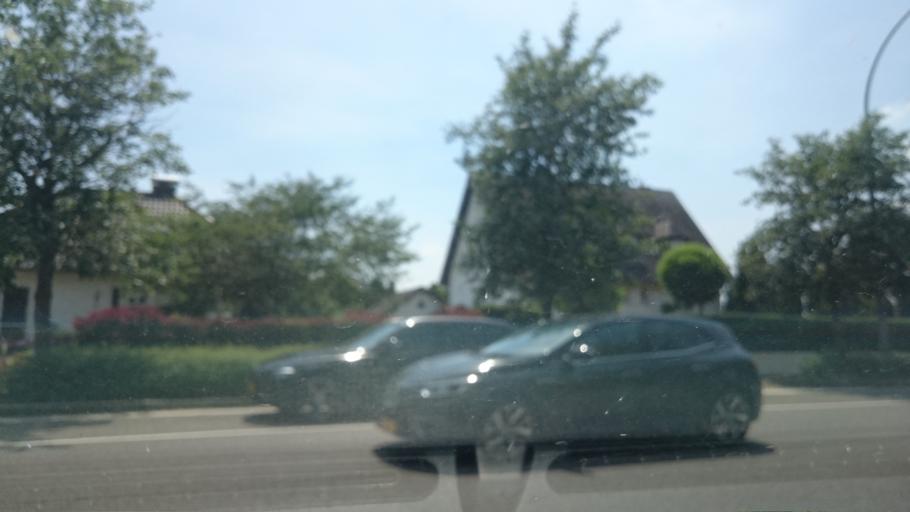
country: LU
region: Luxembourg
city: Capellen
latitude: 49.6463
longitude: 5.9737
